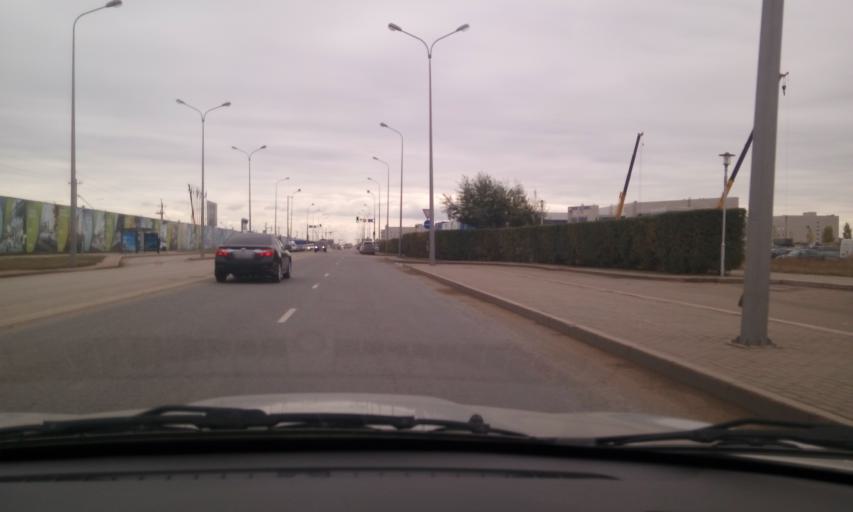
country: KZ
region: Astana Qalasy
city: Astana
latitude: 51.0860
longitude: 71.4046
